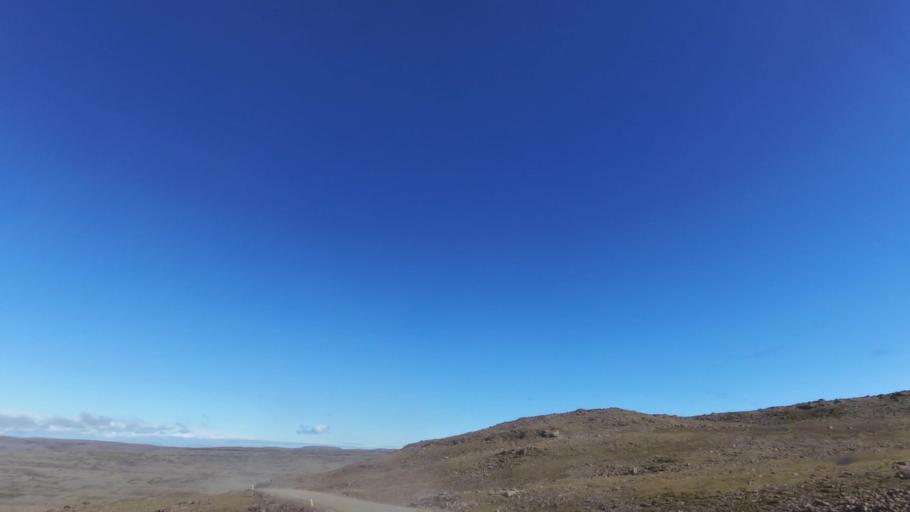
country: IS
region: West
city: Olafsvik
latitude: 65.5540
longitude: -24.2281
